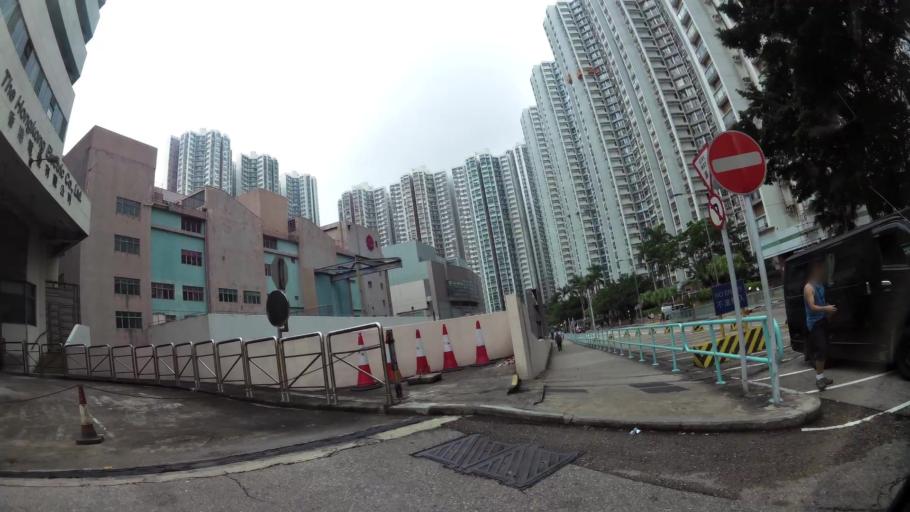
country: HK
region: Central and Western
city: Central
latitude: 22.2443
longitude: 114.1482
